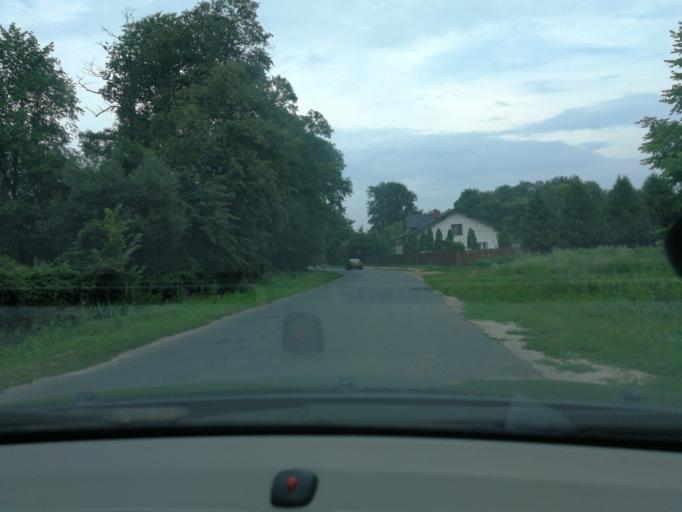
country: PL
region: Masovian Voivodeship
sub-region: Powiat grodziski
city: Grodzisk Mazowiecki
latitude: 52.1309
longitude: 20.5913
